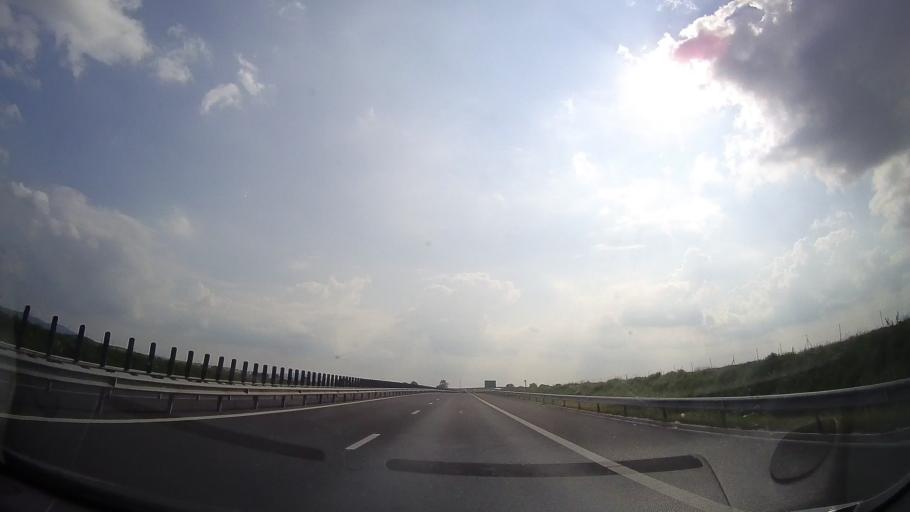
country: RO
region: Timis
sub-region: Comuna Faget
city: Faget
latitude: 45.8346
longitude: 22.2133
